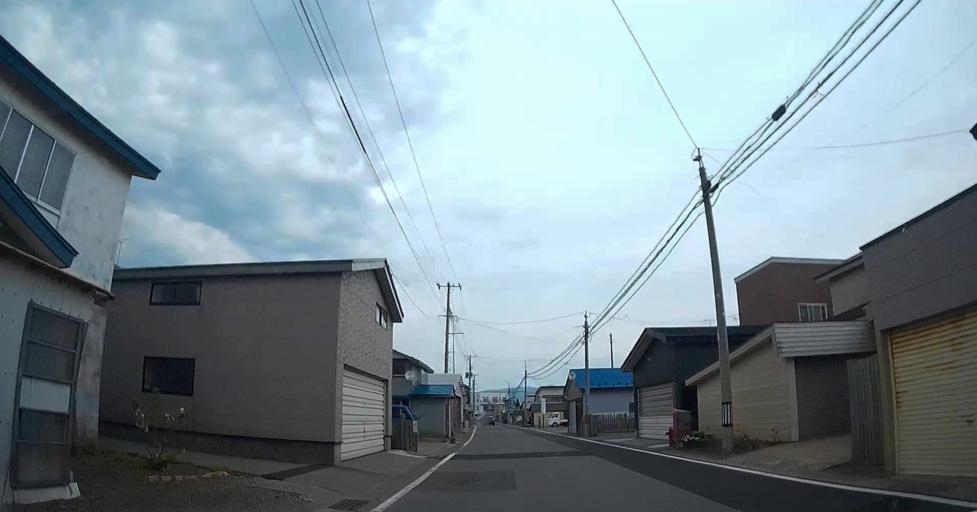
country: JP
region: Aomori
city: Shimokizukuri
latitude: 41.0332
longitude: 140.3287
